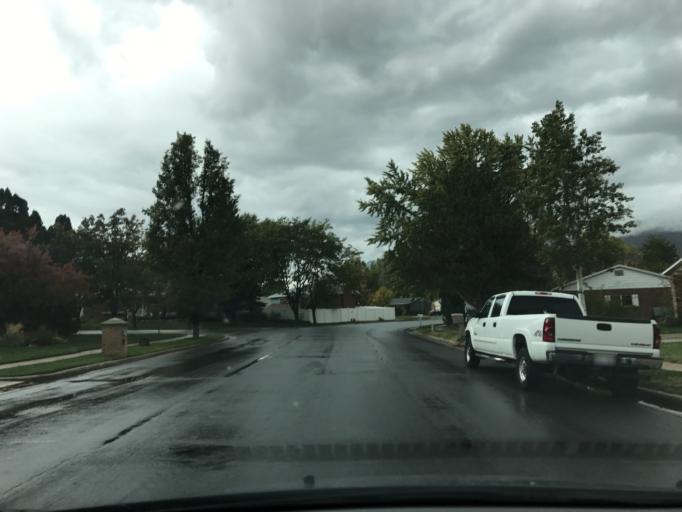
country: US
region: Utah
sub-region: Davis County
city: South Weber
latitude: 41.1095
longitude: -111.9156
